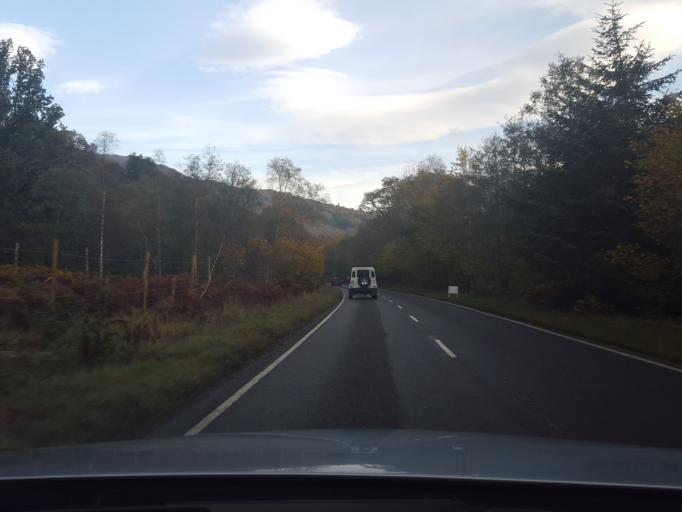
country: GB
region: Scotland
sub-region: Highland
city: Beauly
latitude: 57.2180
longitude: -4.6550
